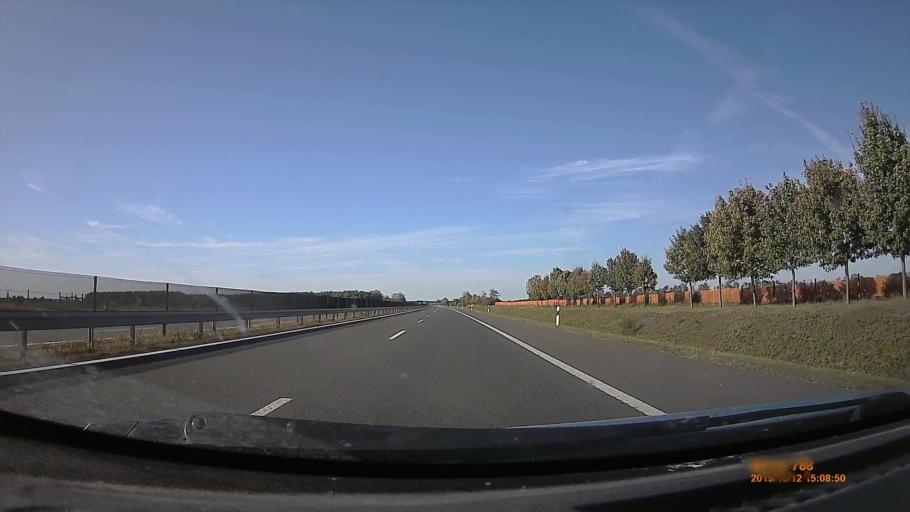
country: HU
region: Hajdu-Bihar
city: Hajduboszormeny
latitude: 47.6388
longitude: 21.5013
